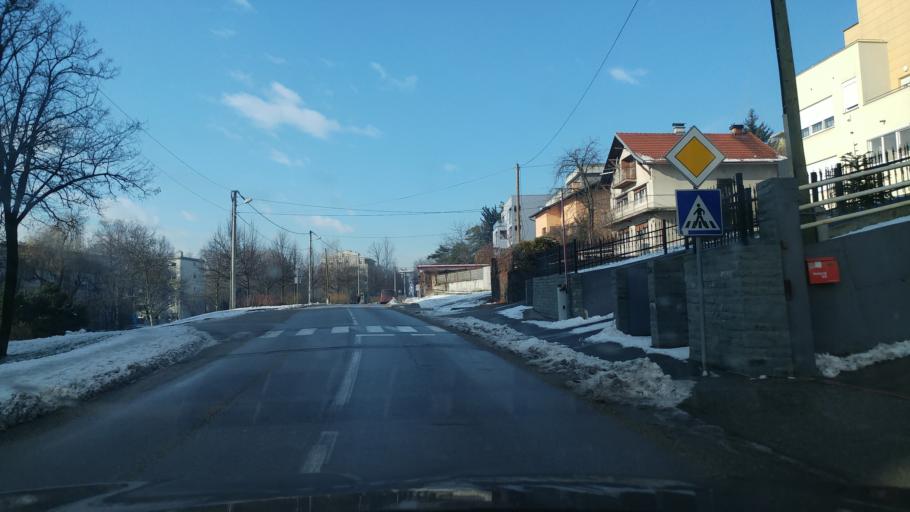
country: HR
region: Grad Zagreb
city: Stenjevec
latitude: 45.8195
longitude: 15.8773
